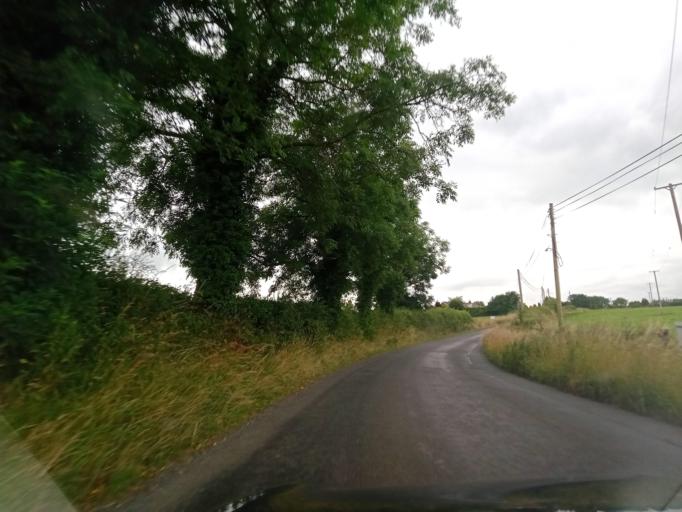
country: IE
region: Leinster
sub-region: Kilkenny
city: Castlecomer
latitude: 52.8942
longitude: -7.1512
